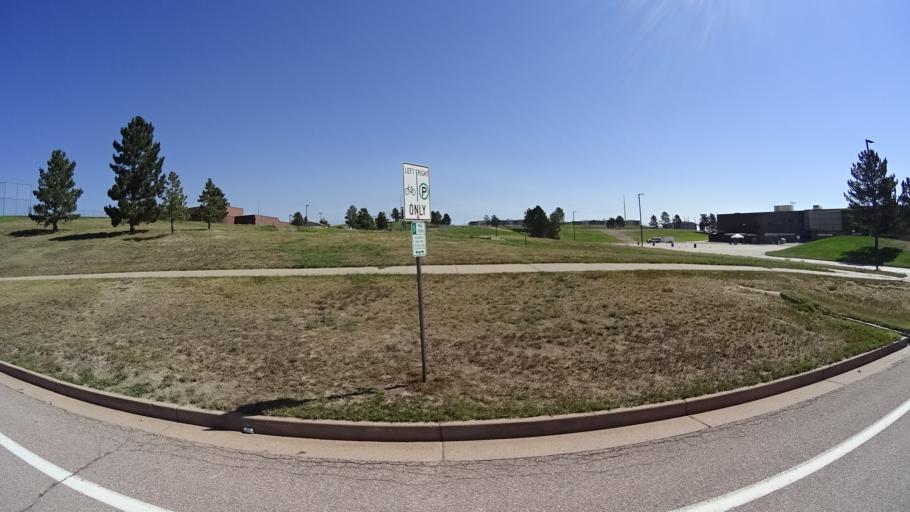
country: US
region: Colorado
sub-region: El Paso County
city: Black Forest
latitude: 38.9595
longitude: -104.7390
